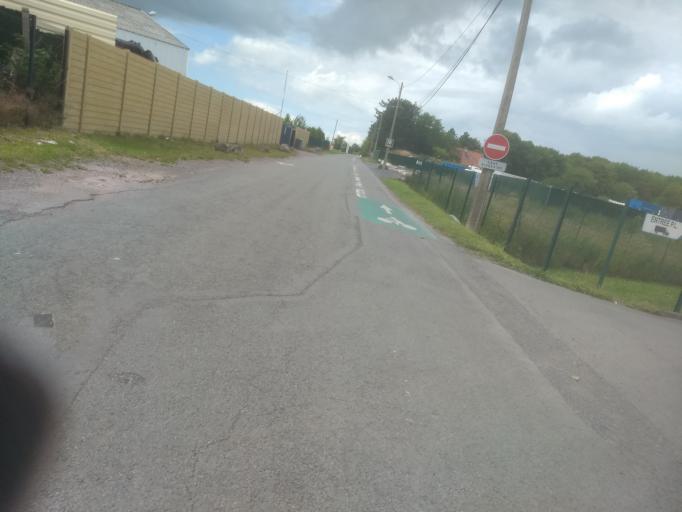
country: FR
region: Nord-Pas-de-Calais
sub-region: Departement du Pas-de-Calais
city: Dainville
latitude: 50.2705
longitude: 2.7211
